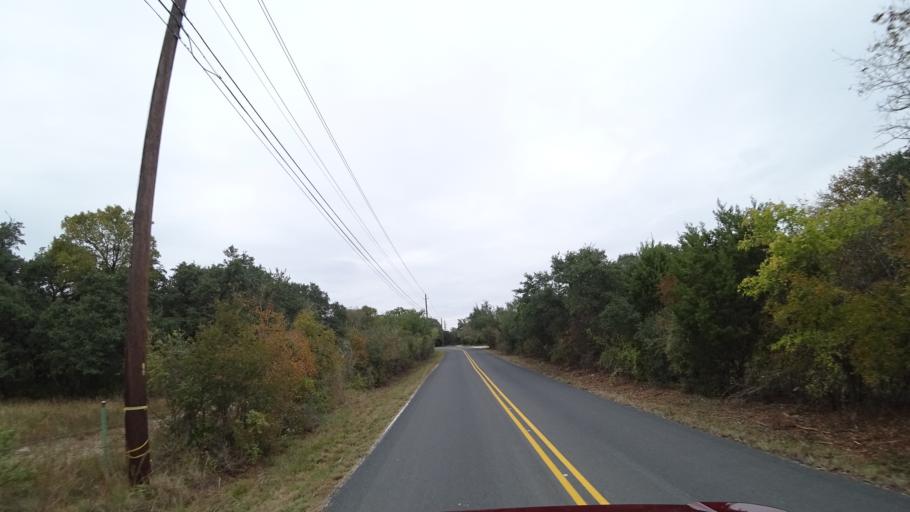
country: US
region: Texas
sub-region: Travis County
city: Wells Branch
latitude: 30.4388
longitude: -97.7076
